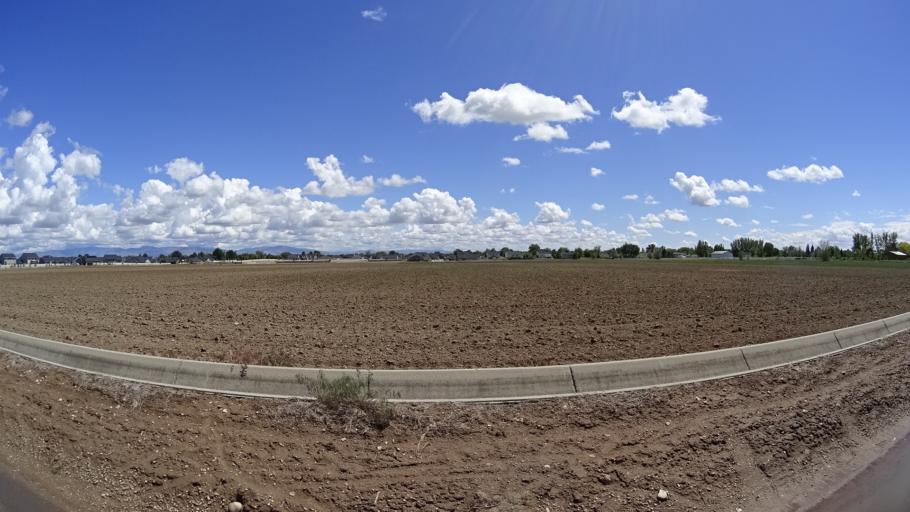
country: US
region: Idaho
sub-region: Ada County
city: Kuna
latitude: 43.5081
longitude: -116.4239
